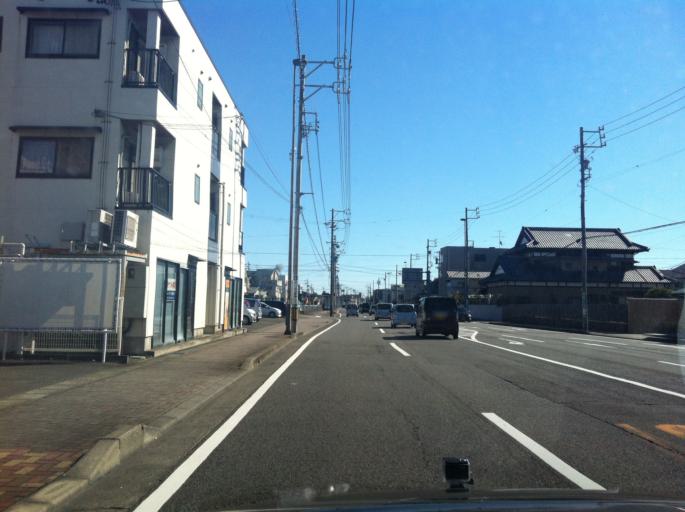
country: JP
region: Shizuoka
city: Shizuoka-shi
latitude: 34.9581
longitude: 138.4016
